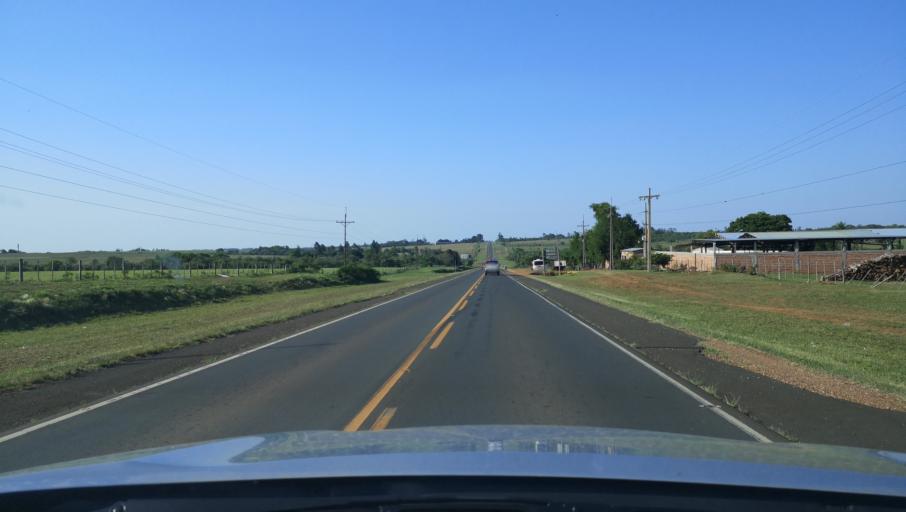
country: PY
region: Misiones
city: Santa Maria
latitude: -26.8381
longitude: -57.0348
